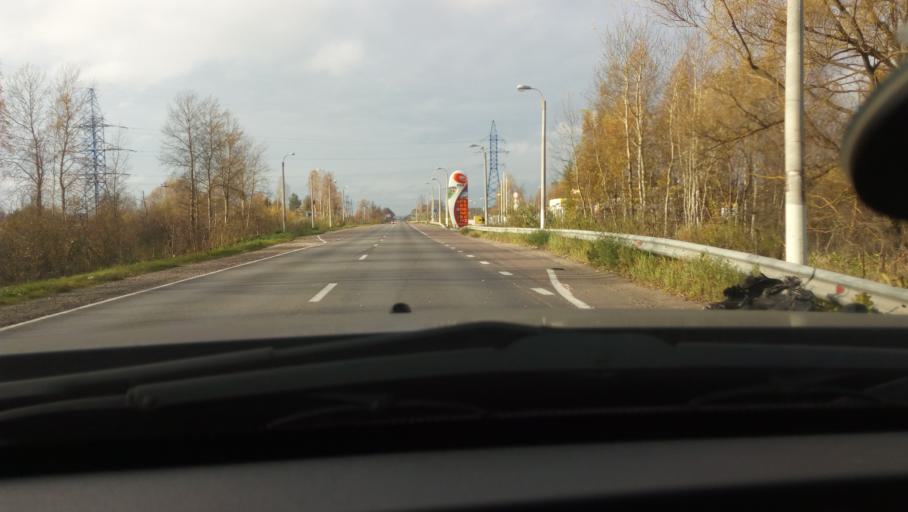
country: RU
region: Moskovskaya
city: Rakhmanovo
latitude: 55.7478
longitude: 38.5837
